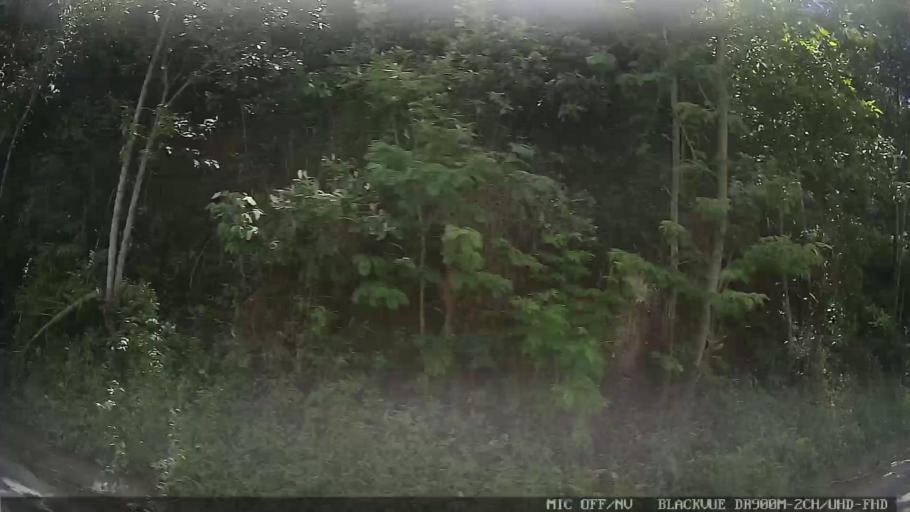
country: BR
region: Sao Paulo
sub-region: Amparo
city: Amparo
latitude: -22.7700
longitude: -46.7383
